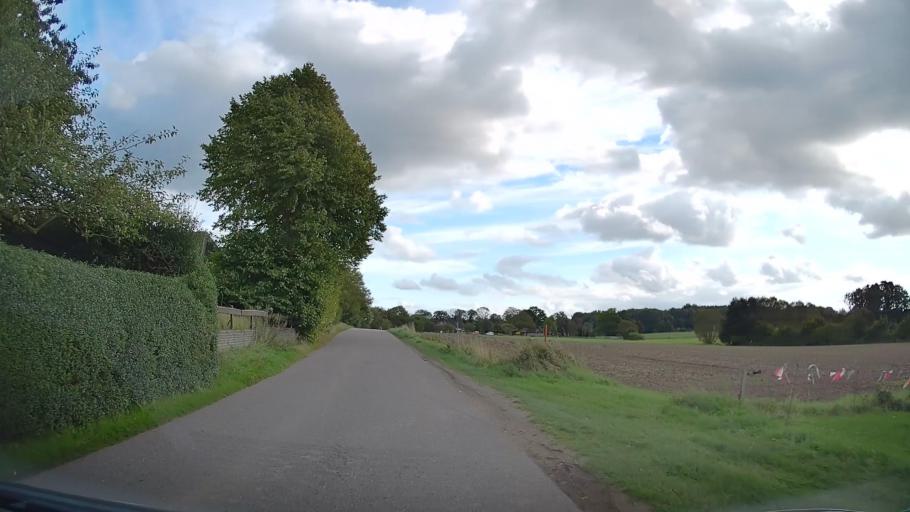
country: DE
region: Schleswig-Holstein
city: Steinberg
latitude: 54.7807
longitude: 9.7809
